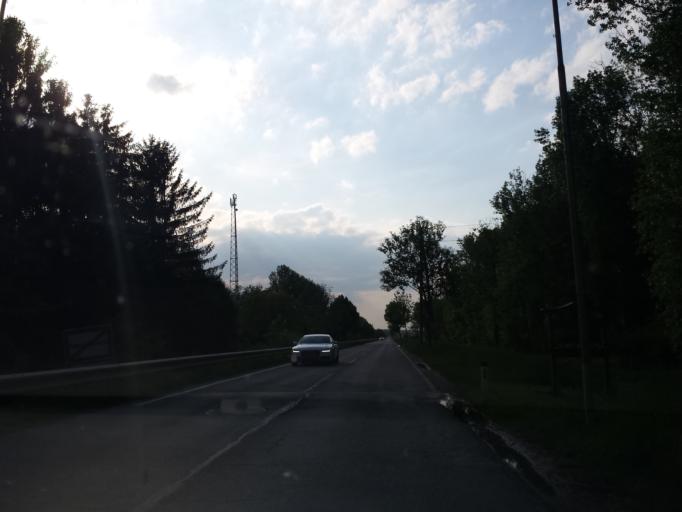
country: AT
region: Lower Austria
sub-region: Politischer Bezirk Ganserndorf
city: Untersiebenbrunn
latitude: 48.2590
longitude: 16.7375
